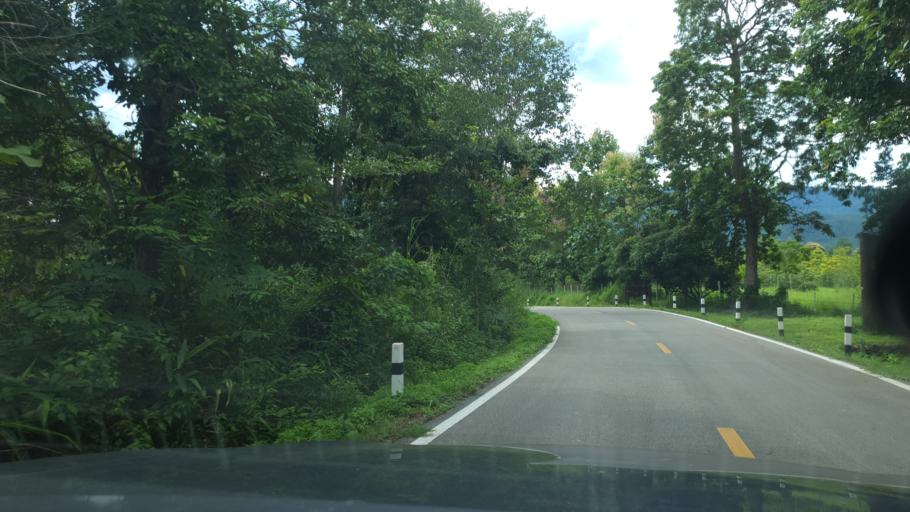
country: TH
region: Lamphun
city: Mae Tha
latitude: 18.5278
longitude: 99.2528
